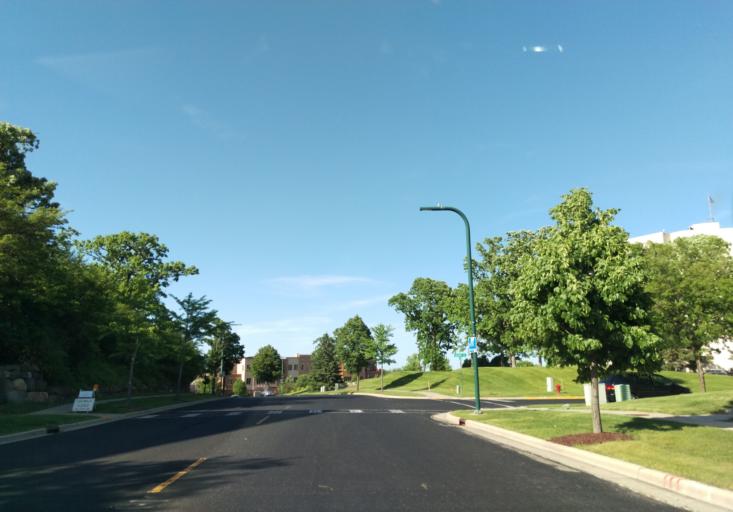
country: US
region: Wisconsin
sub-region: Dane County
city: Middleton
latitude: 43.0881
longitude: -89.5277
